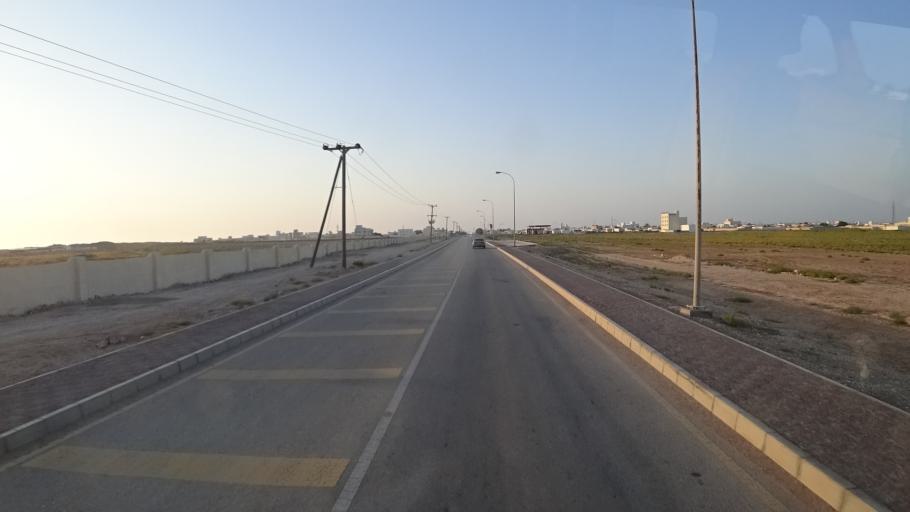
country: OM
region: Ash Sharqiyah
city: Sur
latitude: 22.5103
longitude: 59.7942
